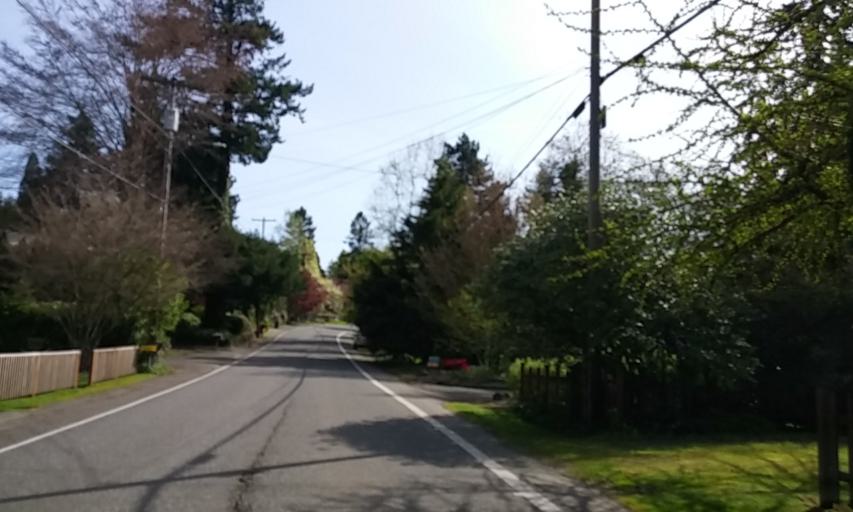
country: US
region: Oregon
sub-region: Washington County
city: West Slope
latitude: 45.5037
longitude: -122.7535
